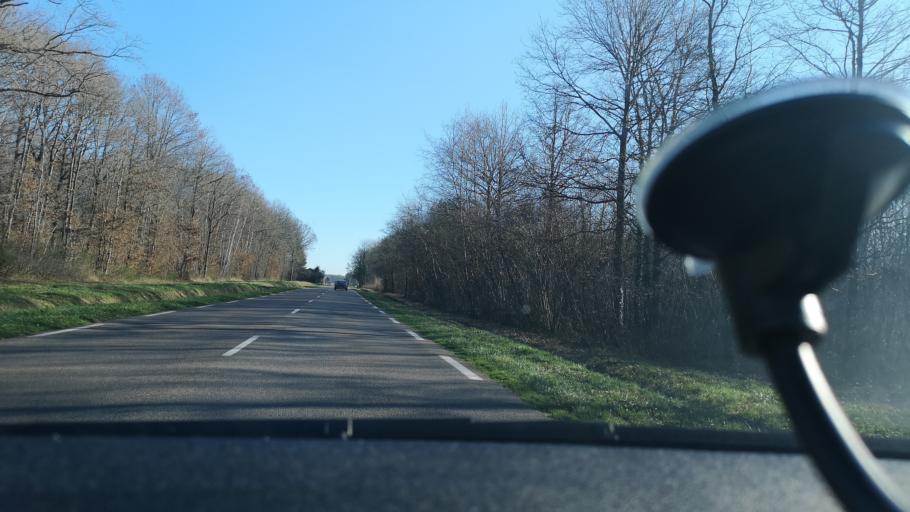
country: FR
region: Bourgogne
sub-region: Departement de Saone-et-Loire
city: Ouroux-sur-Saone
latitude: 46.7751
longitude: 4.9603
